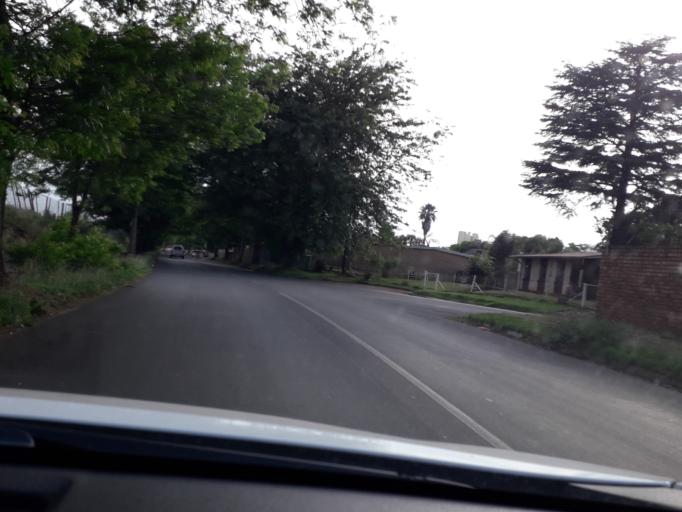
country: ZA
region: Gauteng
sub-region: City of Johannesburg Metropolitan Municipality
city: Johannesburg
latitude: -26.1729
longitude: 27.9703
